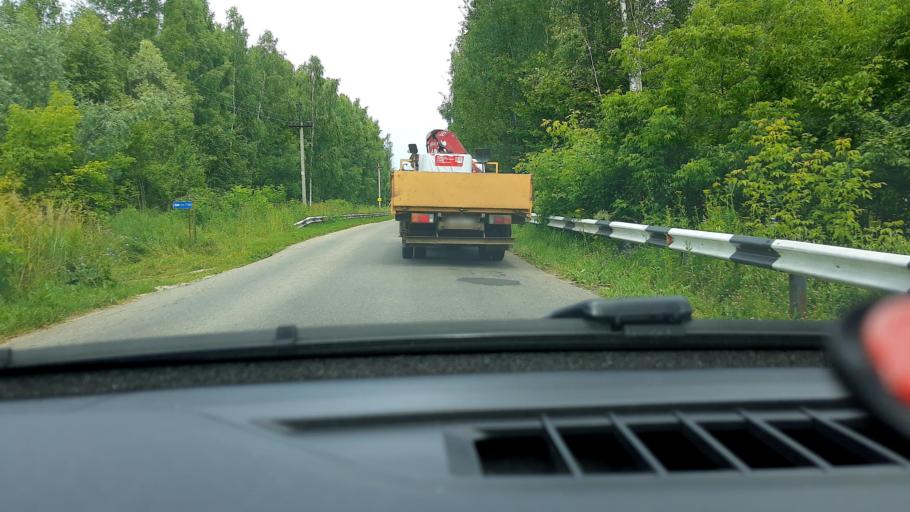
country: RU
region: Nizjnij Novgorod
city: Bogorodsk
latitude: 56.1413
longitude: 43.5885
